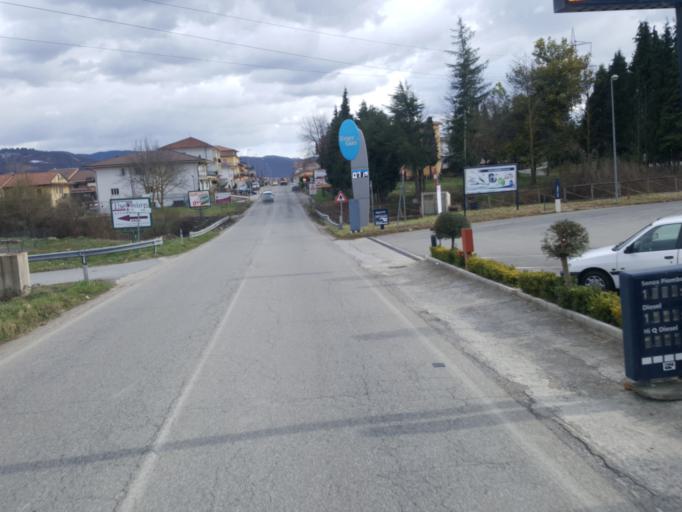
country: IT
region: Calabria
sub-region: Provincia di Cosenza
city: Figline Vegliaturo
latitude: 39.2138
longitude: 16.3082
